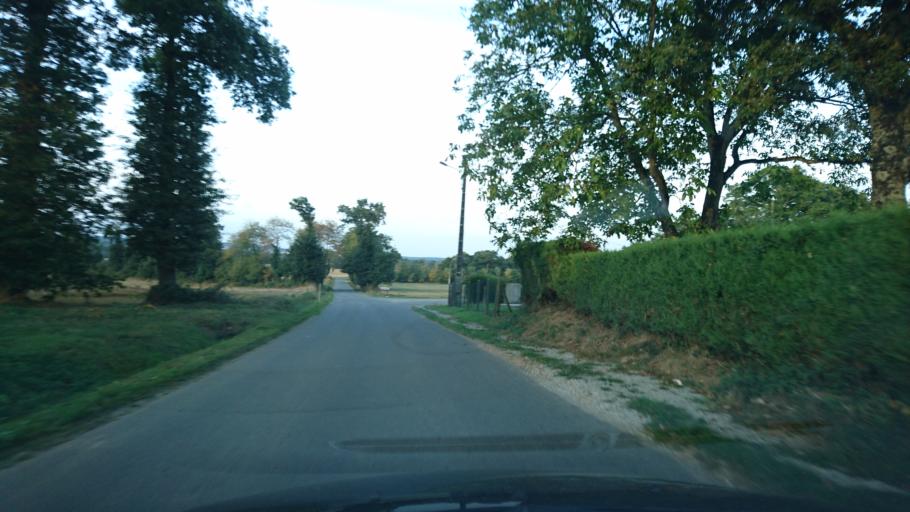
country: FR
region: Brittany
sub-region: Departement d'Ille-et-Vilaine
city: Sixt-sur-Aff
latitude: 47.7780
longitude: -2.0748
